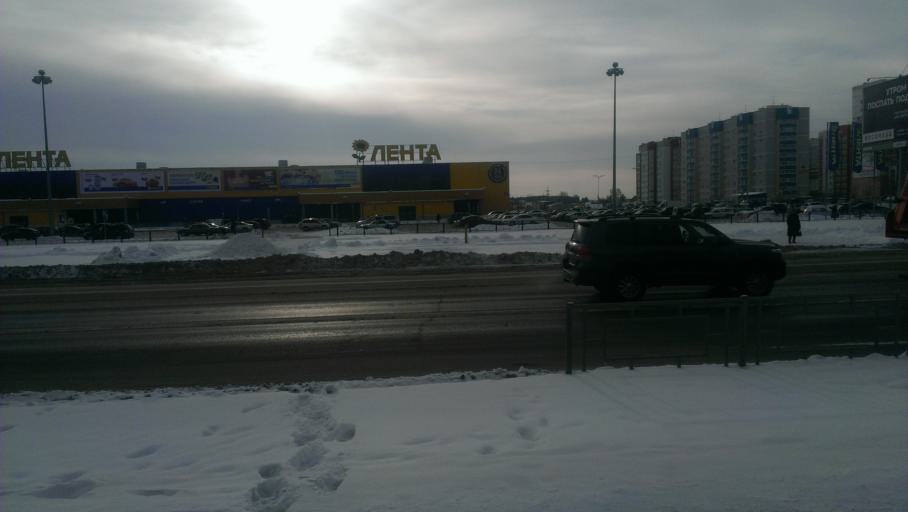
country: RU
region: Altai Krai
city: Novosilikatnyy
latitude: 53.3281
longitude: 83.6848
